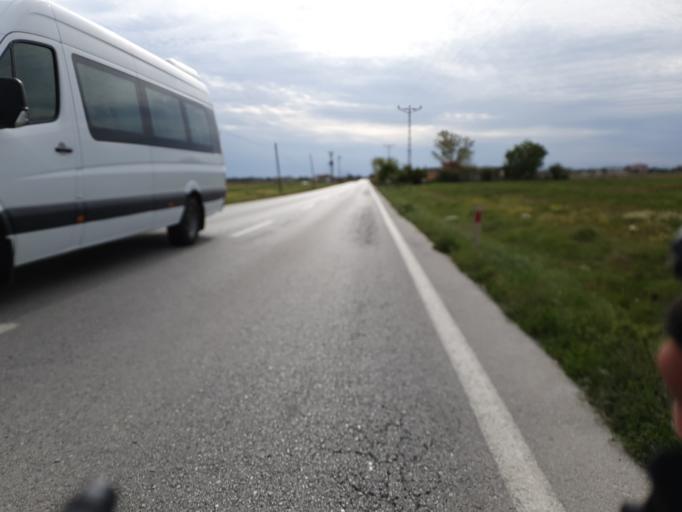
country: TR
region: Tekirdag
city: Velimese
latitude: 41.2907
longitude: 27.9190
